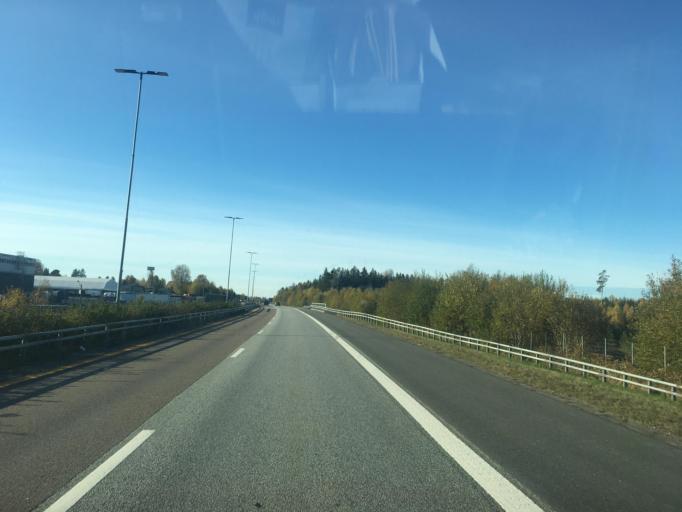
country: NO
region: Ostfold
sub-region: Rade
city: Karlshus
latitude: 59.3552
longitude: 10.8719
